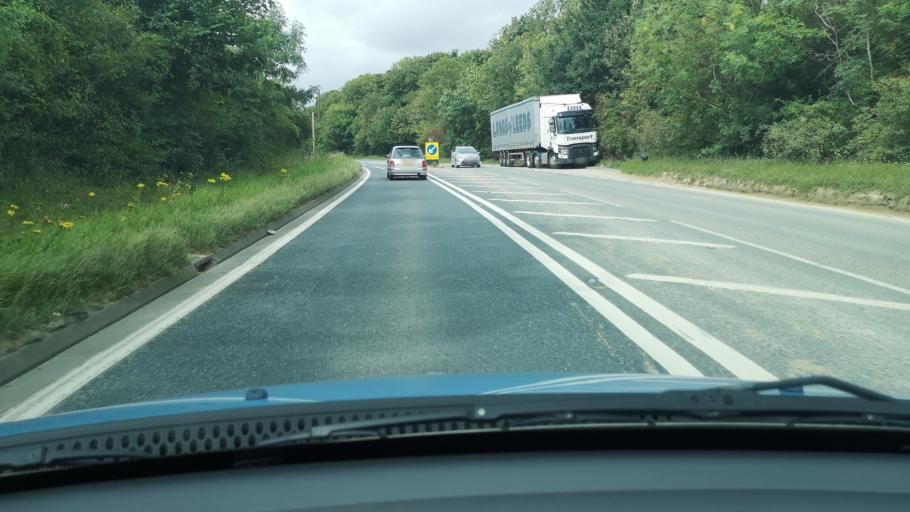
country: GB
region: England
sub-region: City and Borough of Wakefield
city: South Elmsall
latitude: 53.5909
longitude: -1.2463
